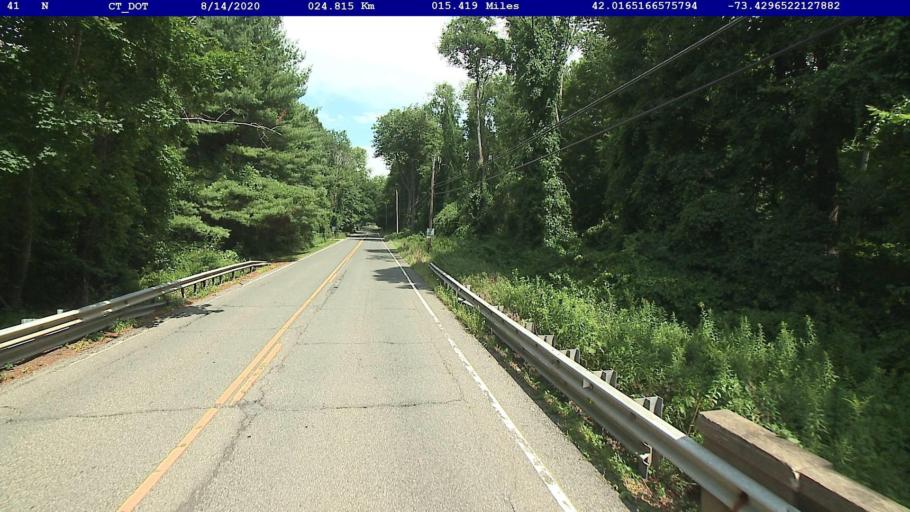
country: US
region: Connecticut
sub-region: Litchfield County
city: Canaan
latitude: 42.0165
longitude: -73.4297
